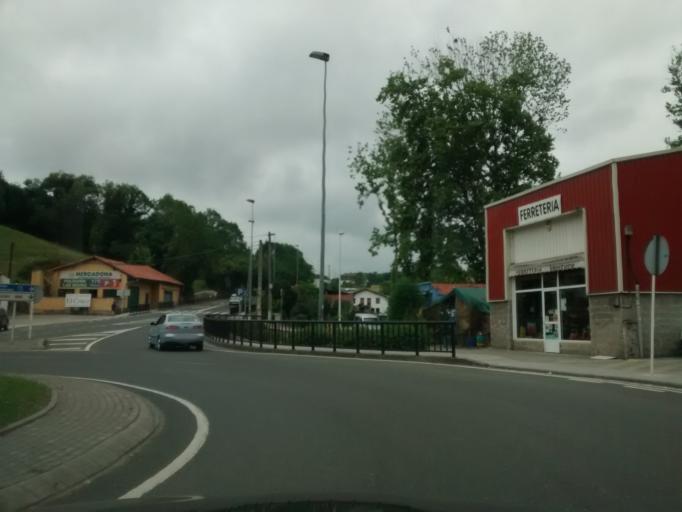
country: ES
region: Cantabria
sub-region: Provincia de Cantabria
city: Cabezon de la Sal
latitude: 43.3092
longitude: -4.2376
